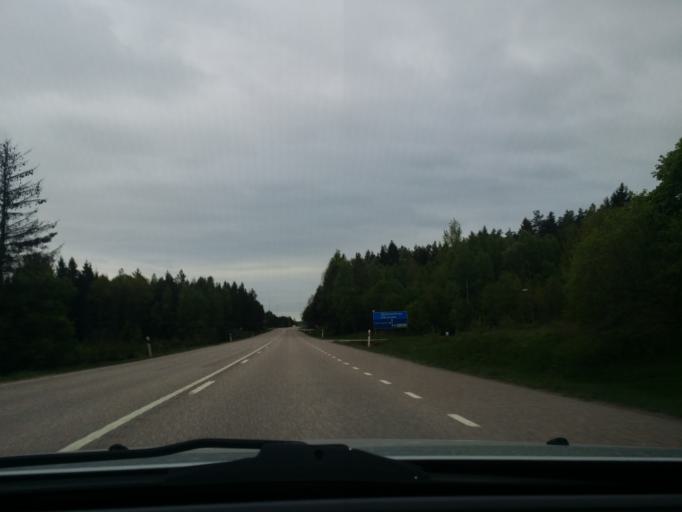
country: SE
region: Vaestmanland
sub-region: Hallstahammars Kommun
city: Kolback
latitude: 59.5700
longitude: 16.3507
